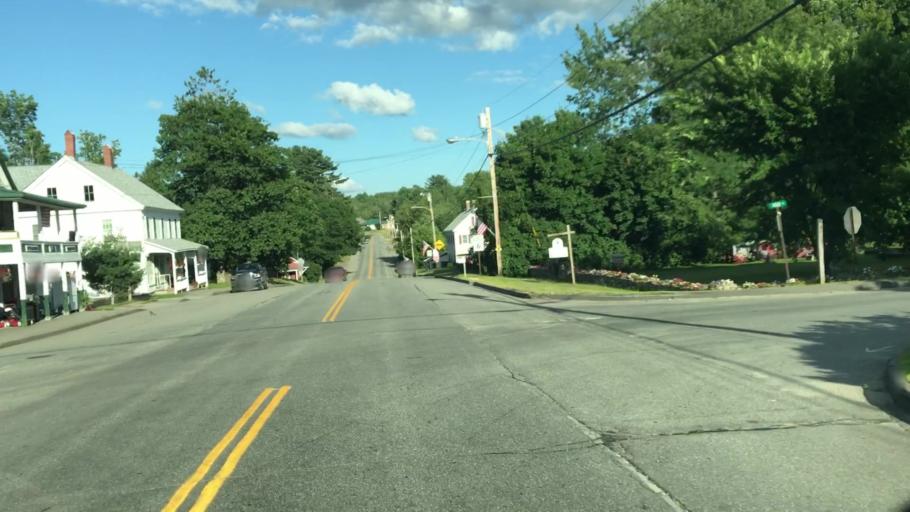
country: US
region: Maine
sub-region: Penobscot County
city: Lincoln
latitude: 45.3601
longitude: -68.2864
